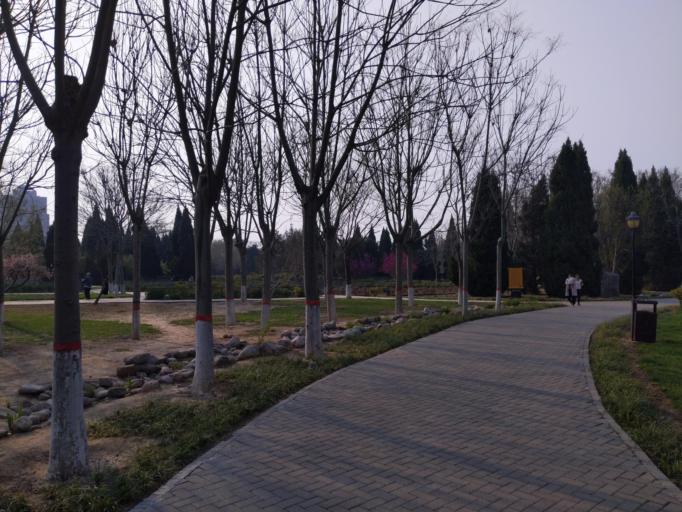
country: CN
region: Henan Sheng
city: Puyang
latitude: 35.7510
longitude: 115.0247
